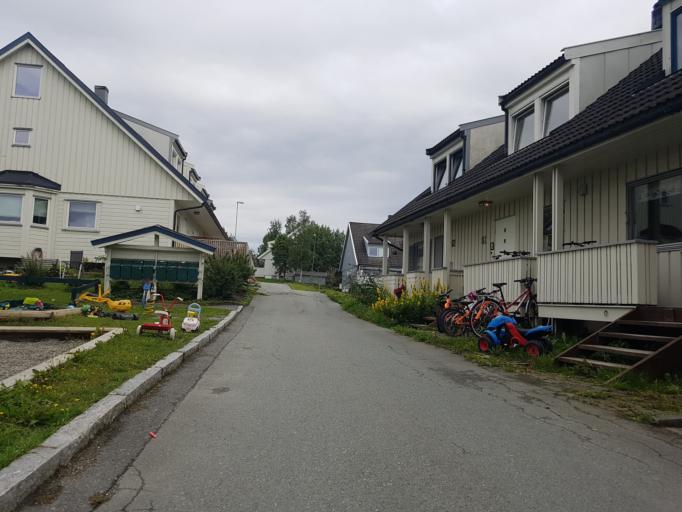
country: NO
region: Sor-Trondelag
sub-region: Trondheim
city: Trondheim
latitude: 63.3863
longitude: 10.4003
